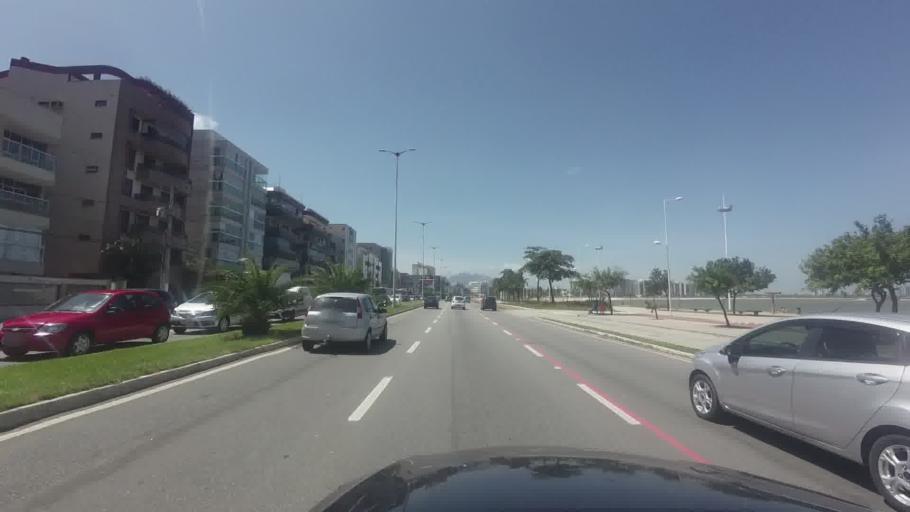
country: BR
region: Espirito Santo
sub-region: Vila Velha
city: Vila Velha
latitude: -20.2904
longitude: -40.2904
